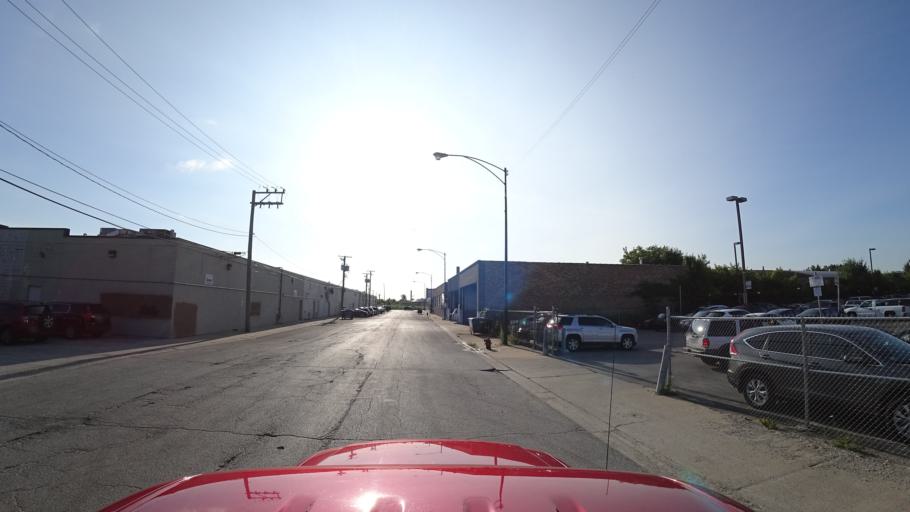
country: US
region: Illinois
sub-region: Cook County
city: Cicero
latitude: 41.8056
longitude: -87.7058
